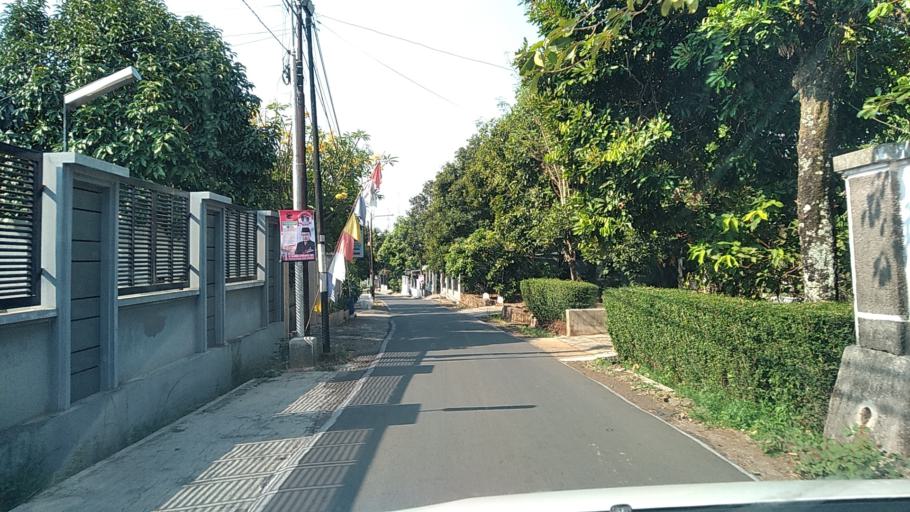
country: ID
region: Central Java
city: Semarang
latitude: -7.0603
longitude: 110.4214
